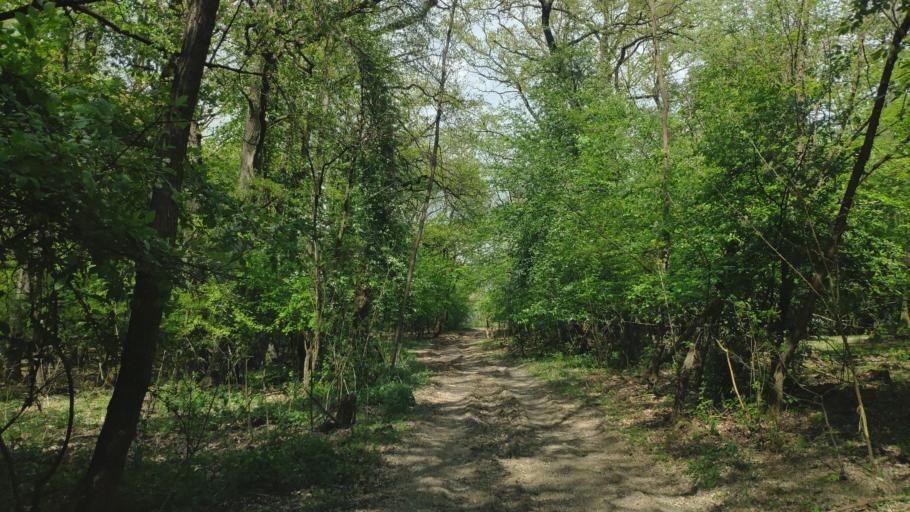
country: SK
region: Kosicky
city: Moldava nad Bodvou
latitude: 48.5537
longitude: 20.9451
